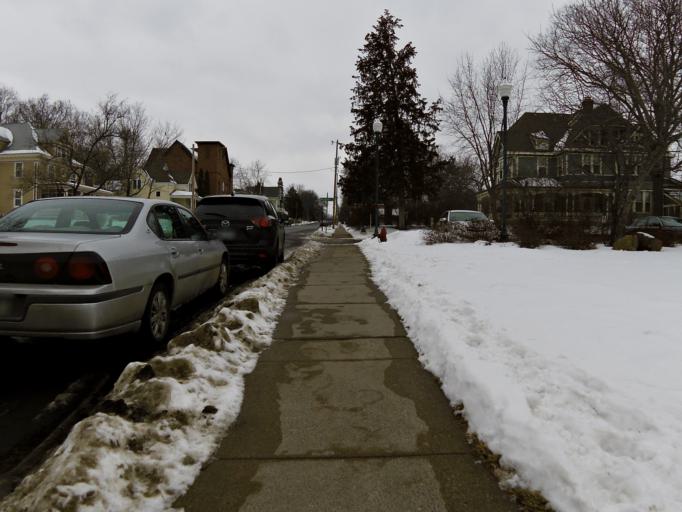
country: US
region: Minnesota
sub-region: Washington County
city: Stillwater
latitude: 45.0575
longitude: -92.8108
